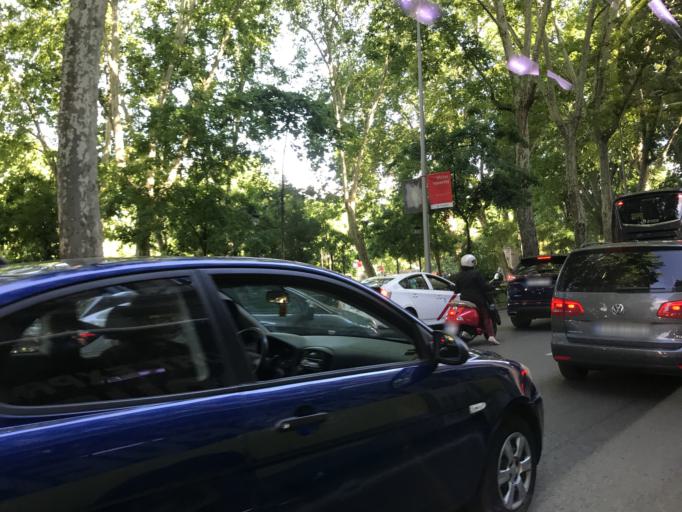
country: ES
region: Madrid
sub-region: Provincia de Madrid
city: Madrid
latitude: 40.4180
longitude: -3.6941
